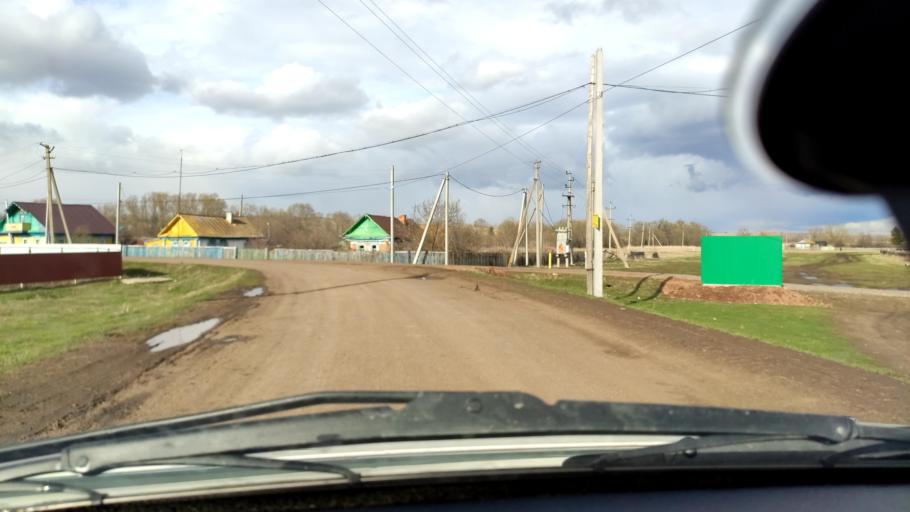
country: RU
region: Bashkortostan
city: Buzdyak
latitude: 54.7688
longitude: 54.6249
